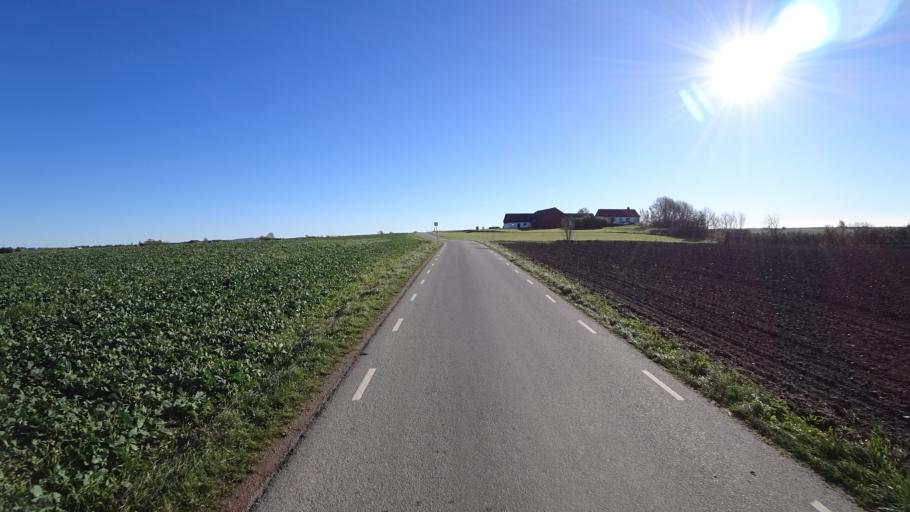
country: SE
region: Skane
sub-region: Svedala Kommun
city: Klagerup
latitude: 55.6165
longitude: 13.2820
